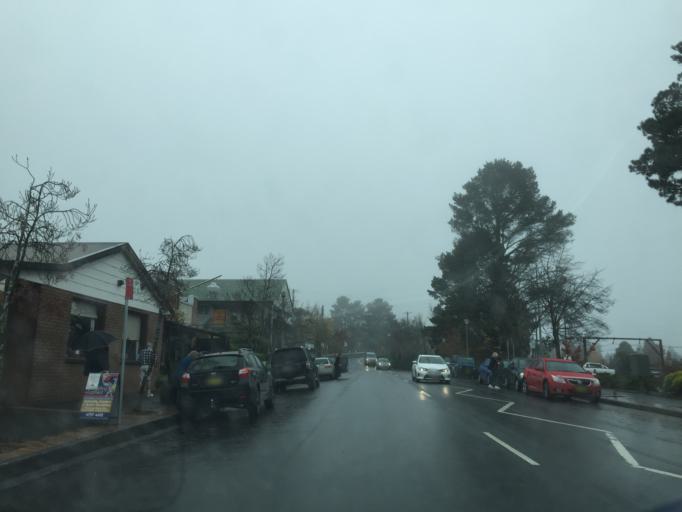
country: AU
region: New South Wales
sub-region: Blue Mountains Municipality
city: Leura
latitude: -33.7092
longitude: 150.3759
